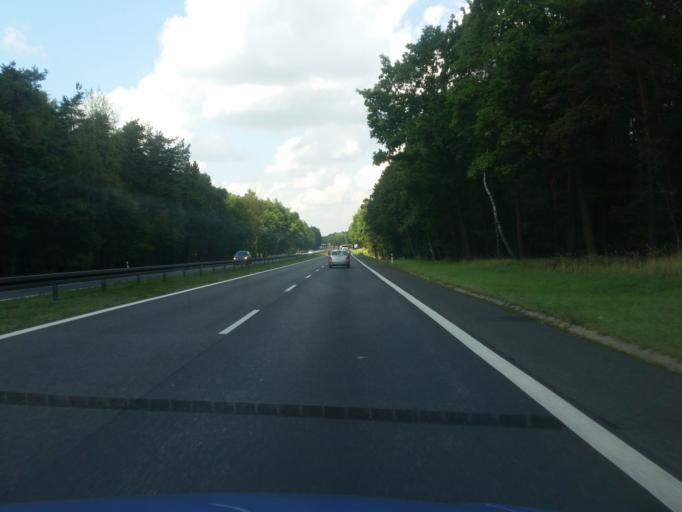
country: PL
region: Silesian Voivodeship
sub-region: Powiat czestochowski
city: Kamienica Polska
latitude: 50.6524
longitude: 19.1325
